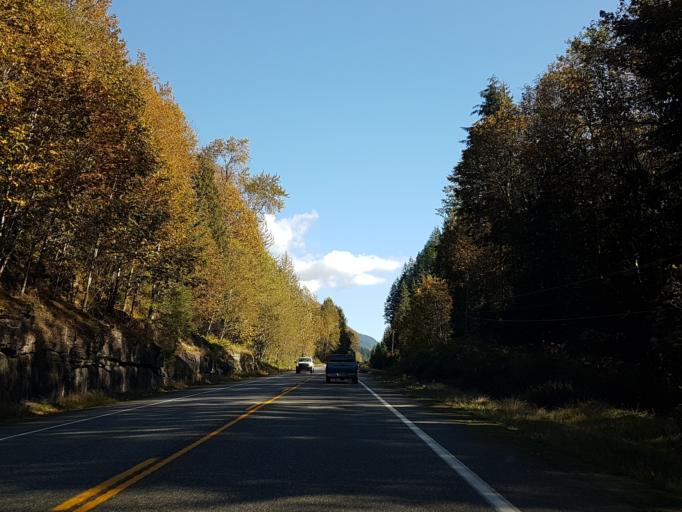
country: US
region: Washington
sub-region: Snohomish County
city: Gold Bar
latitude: 47.8072
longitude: -121.5330
